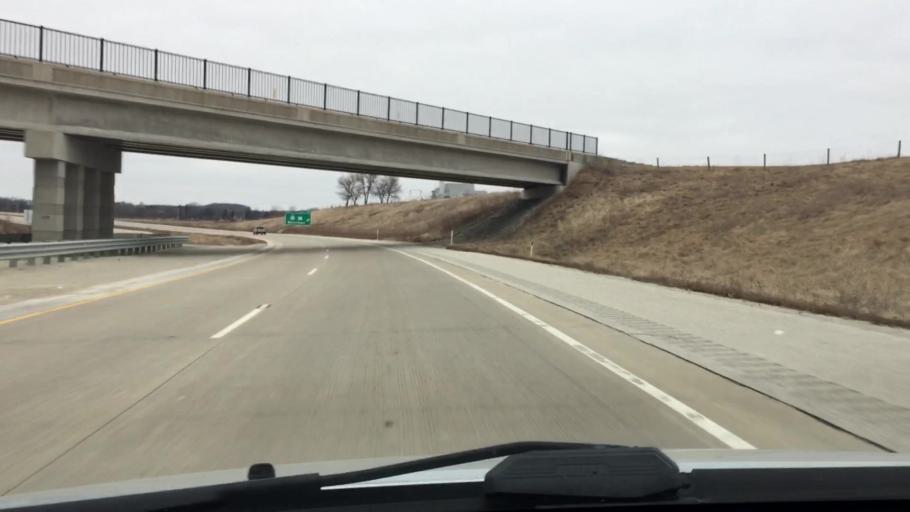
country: US
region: Wisconsin
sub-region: Jefferson County
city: Watertown
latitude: 43.1508
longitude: -88.7351
